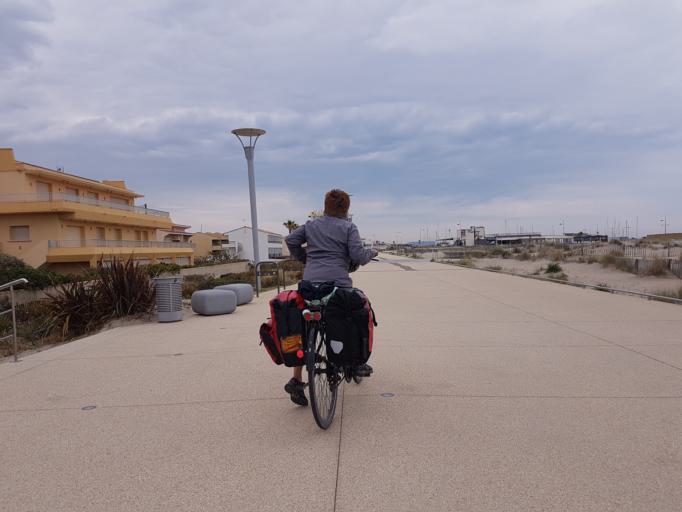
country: FR
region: Languedoc-Roussillon
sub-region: Departement de l'Herault
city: Marseillan
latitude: 43.3165
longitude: 3.5541
